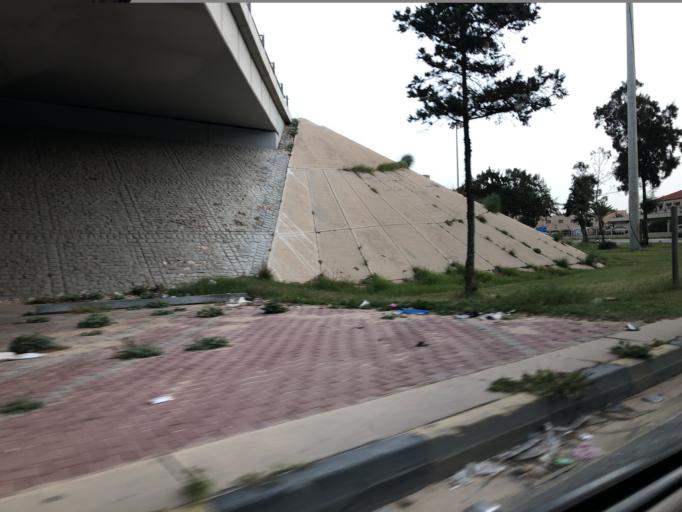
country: LY
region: Tripoli
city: Tripoli
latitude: 32.8673
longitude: 13.1364
